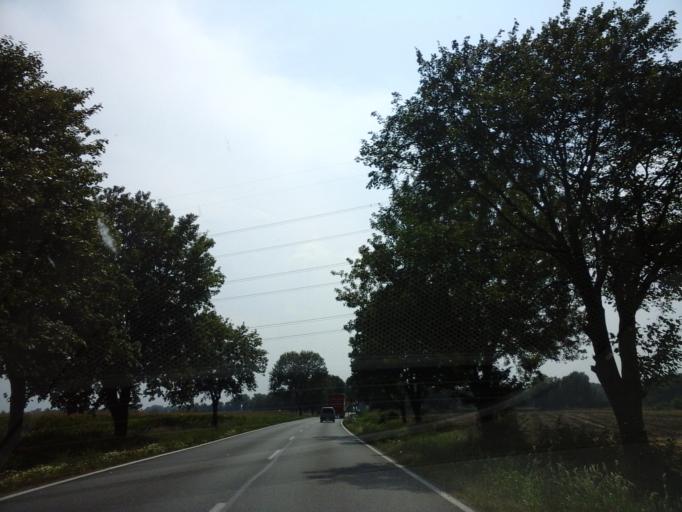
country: PL
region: Lower Silesian Voivodeship
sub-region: Powiat wroclawski
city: Zorawina
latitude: 50.9504
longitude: 17.0708
